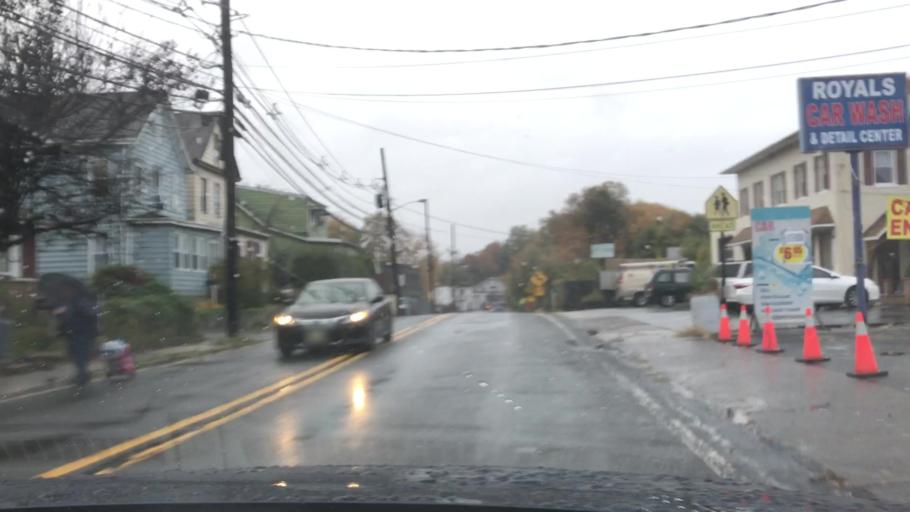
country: US
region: New Jersey
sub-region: Bergen County
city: Wallington
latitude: 40.8637
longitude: -74.0994
